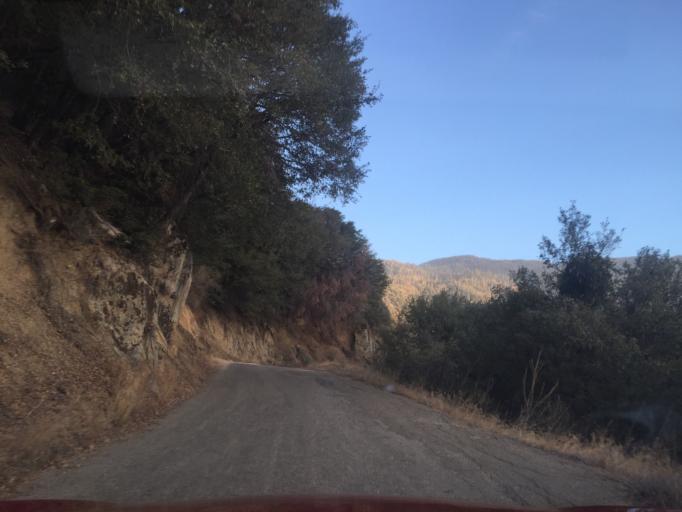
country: US
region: California
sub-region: Tulare County
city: Three Rivers
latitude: 36.4349
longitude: -118.7413
